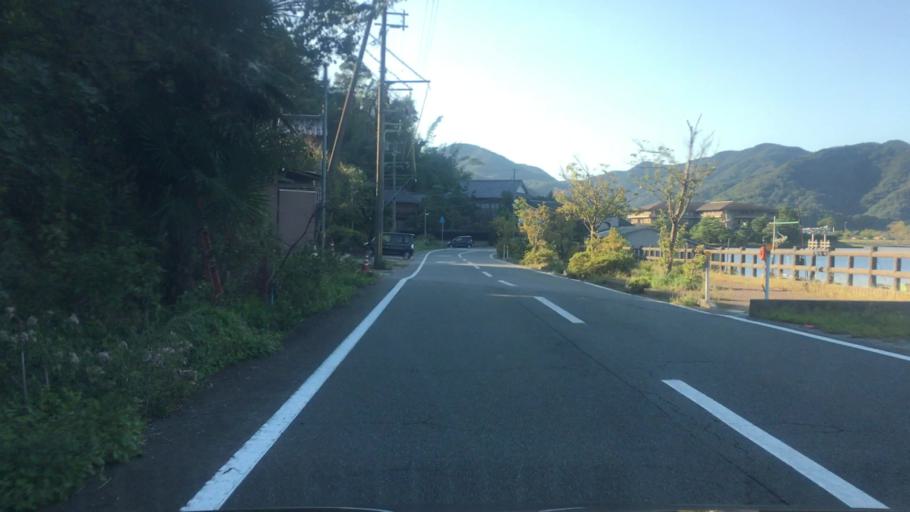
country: JP
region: Hyogo
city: Toyooka
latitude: 35.6178
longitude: 134.8225
